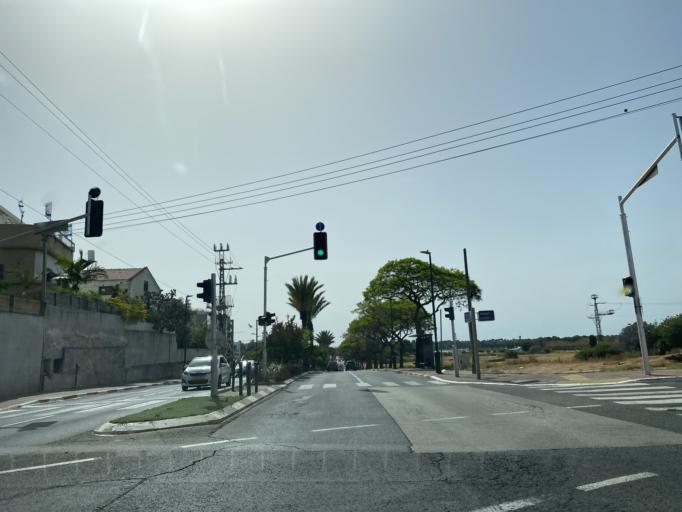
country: IL
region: Tel Aviv
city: Herzliyya
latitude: 32.1767
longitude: 34.8456
